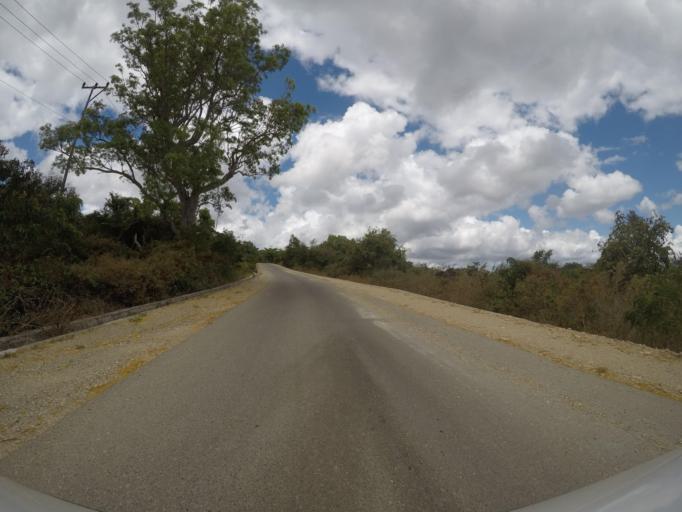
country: TL
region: Lautem
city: Lospalos
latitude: -8.3697
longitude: 126.9267
